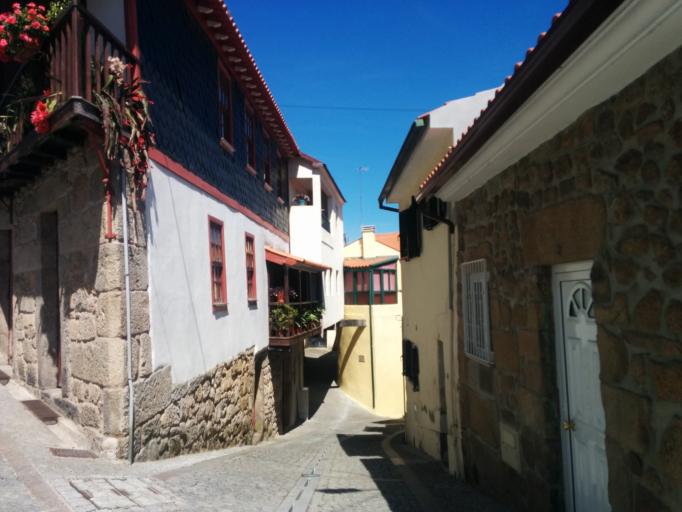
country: PT
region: Viseu
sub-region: Tarouca
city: Tarouca
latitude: 41.0458
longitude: -7.7448
